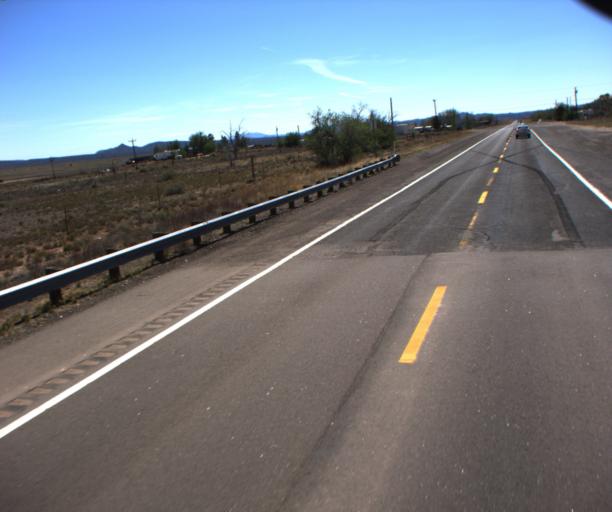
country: US
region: Arizona
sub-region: Mohave County
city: Peach Springs
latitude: 35.4863
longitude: -113.5604
